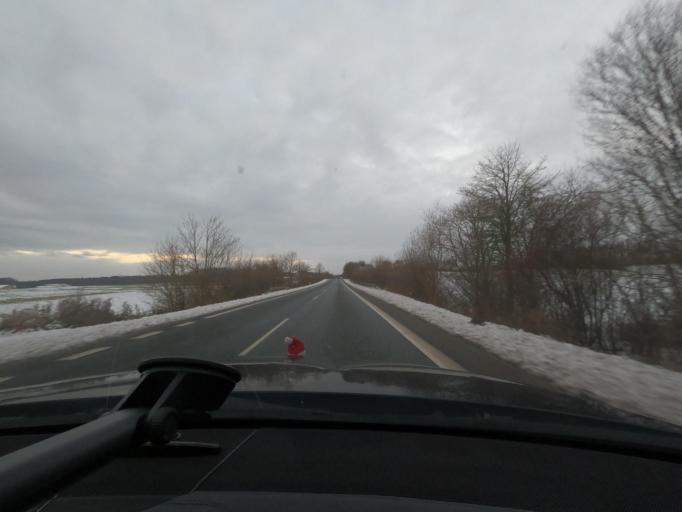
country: DE
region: Schleswig-Holstein
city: Glucksburg
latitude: 54.8885
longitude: 9.5090
